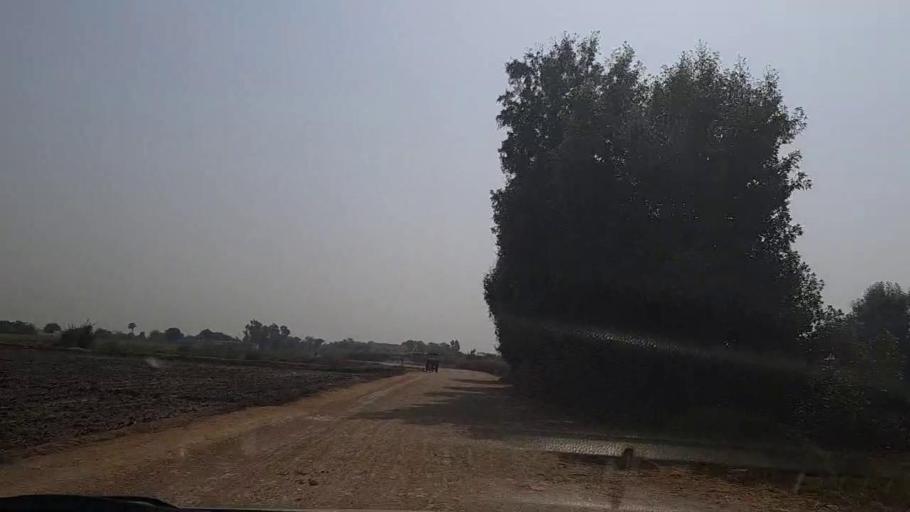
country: PK
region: Sindh
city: Pithoro
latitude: 25.5512
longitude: 69.2486
